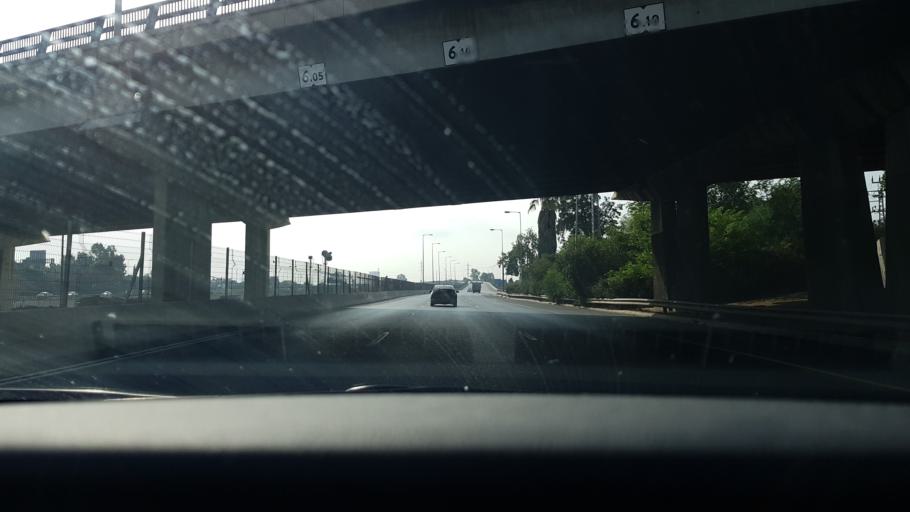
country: IL
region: Tel Aviv
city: Azor
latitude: 32.0472
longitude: 34.7862
